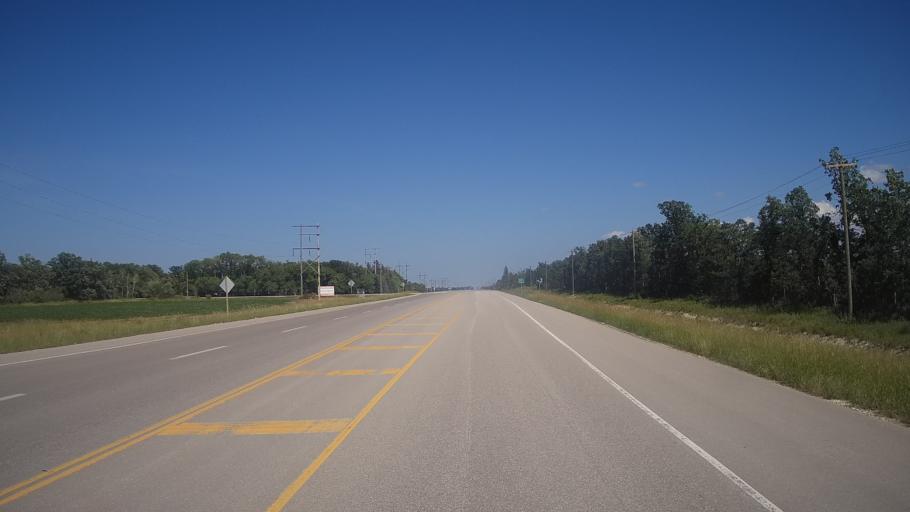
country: CA
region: Manitoba
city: Stonewall
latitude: 50.1228
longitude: -97.3368
